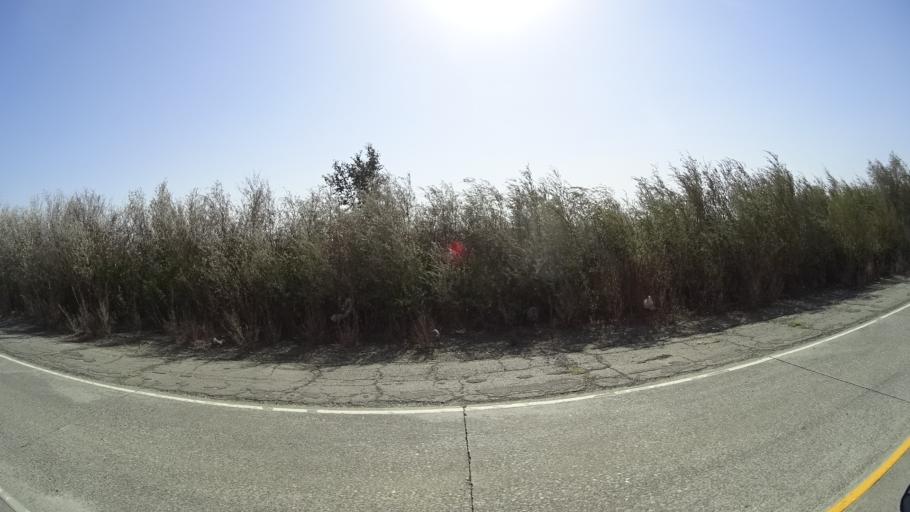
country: US
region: California
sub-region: Yolo County
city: Woodland
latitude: 38.6767
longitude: -121.6619
